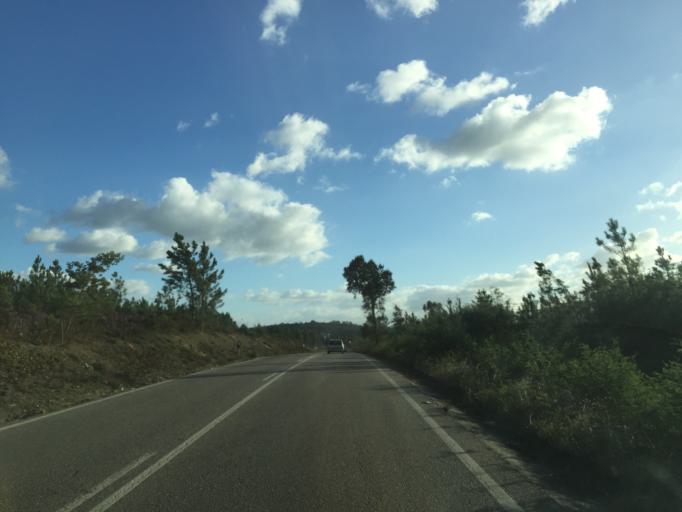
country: PT
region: Leiria
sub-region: Leiria
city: Monte Redondo
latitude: 39.8741
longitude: -8.8388
